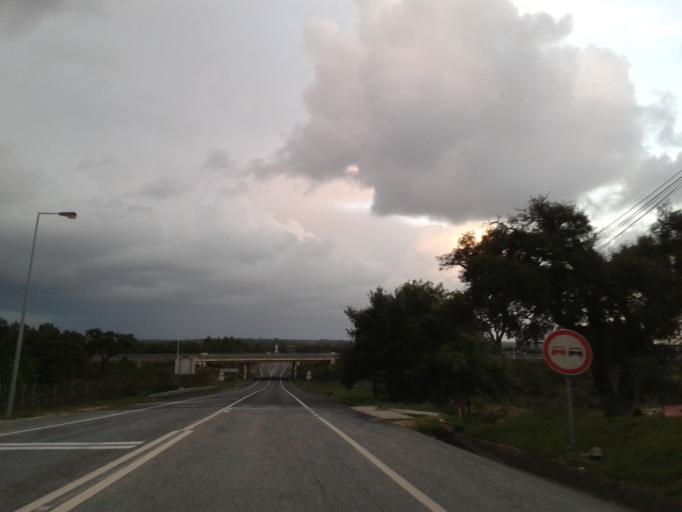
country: PT
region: Santarem
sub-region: Benavente
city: Poceirao
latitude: 38.8390
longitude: -8.7342
